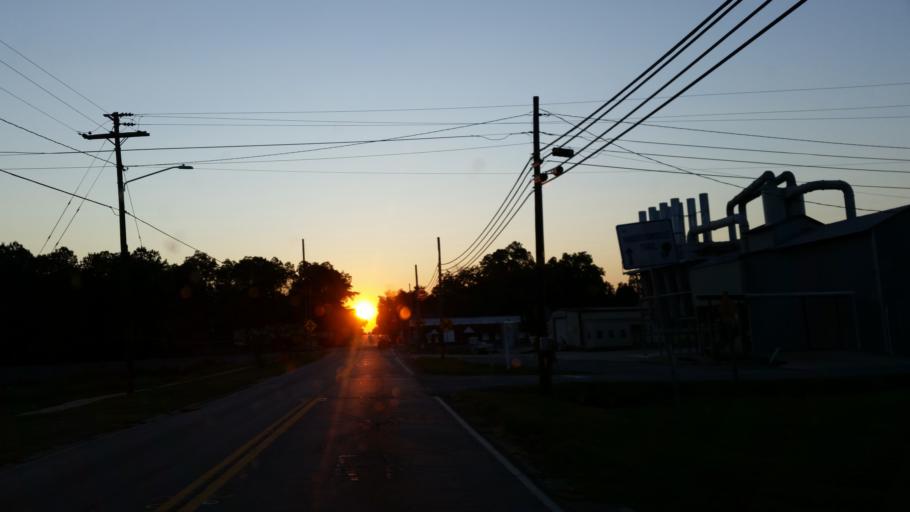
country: US
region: Georgia
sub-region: Dooly County
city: Vienna
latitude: 32.0904
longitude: -83.7861
